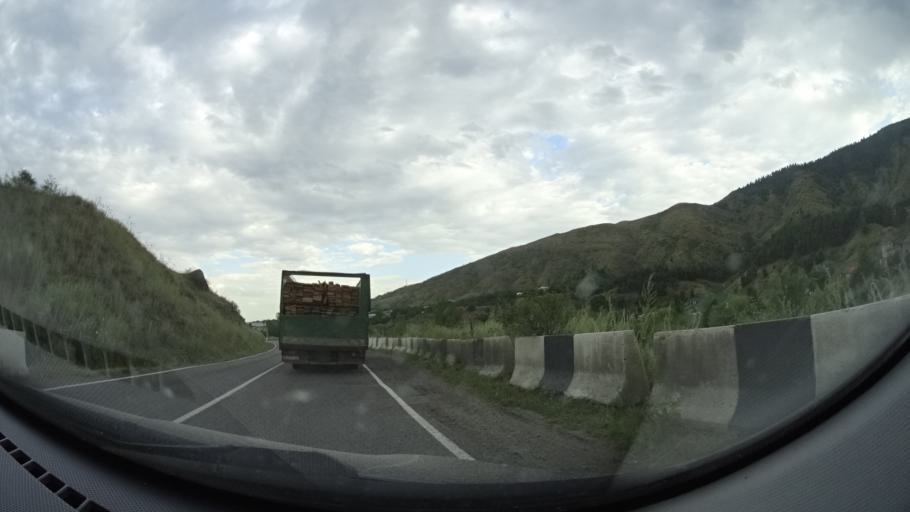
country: GE
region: Samtskhe-Javakheti
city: Akhaltsikhe
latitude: 41.6409
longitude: 42.9687
